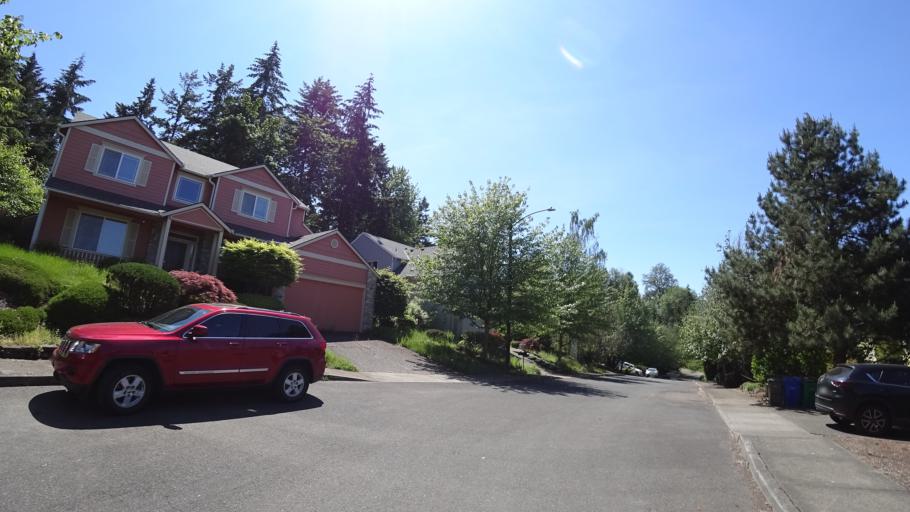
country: US
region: Oregon
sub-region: Clackamas County
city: Lake Oswego
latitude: 45.4504
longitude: -122.7086
